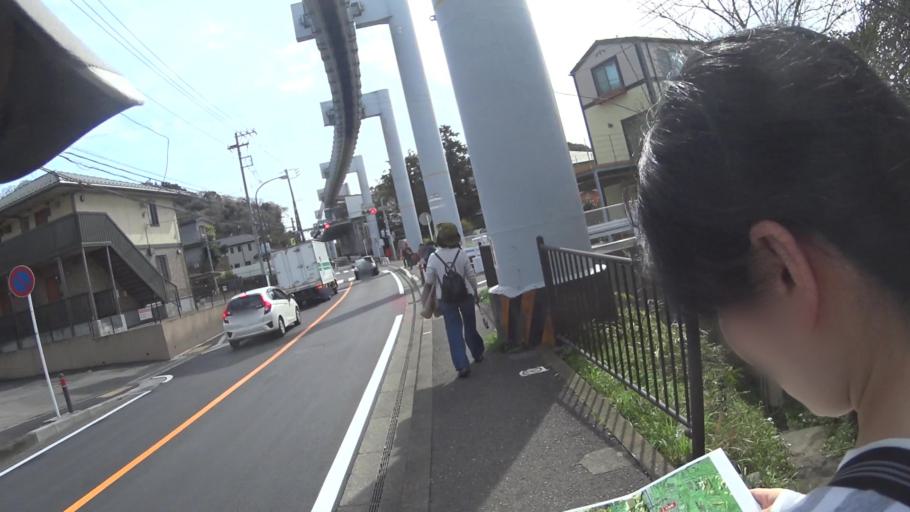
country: JP
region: Kanagawa
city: Kamakura
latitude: 35.3389
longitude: 139.5230
